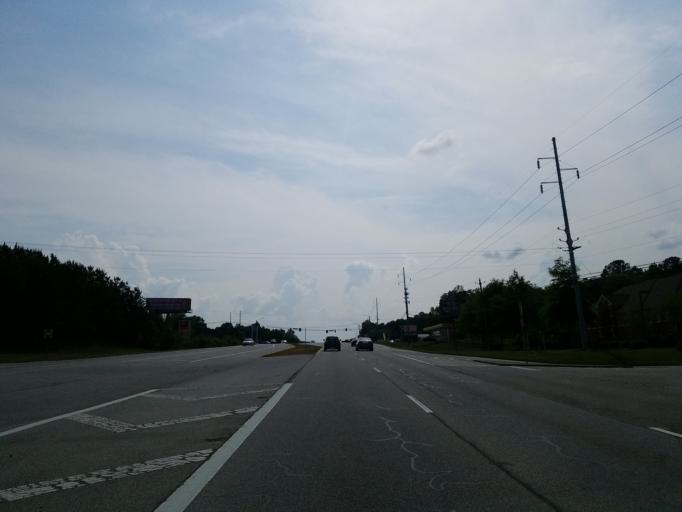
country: US
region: Georgia
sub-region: Paulding County
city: Hiram
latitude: 33.9273
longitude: -84.7454
